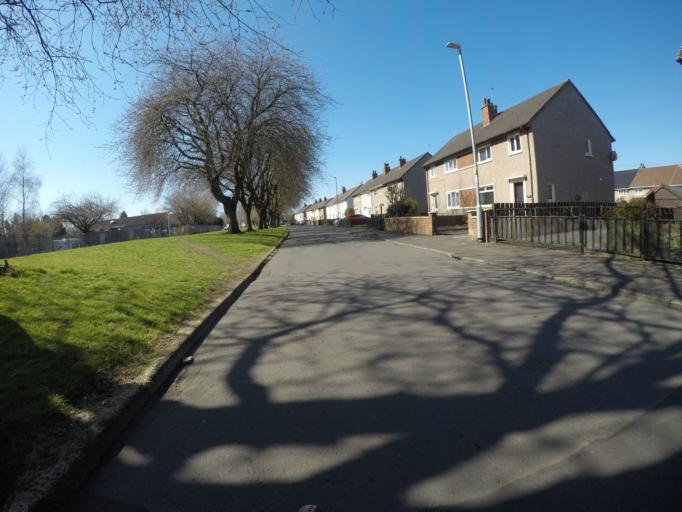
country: GB
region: Scotland
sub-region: North Ayrshire
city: Irvine
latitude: 55.6235
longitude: -4.6515
